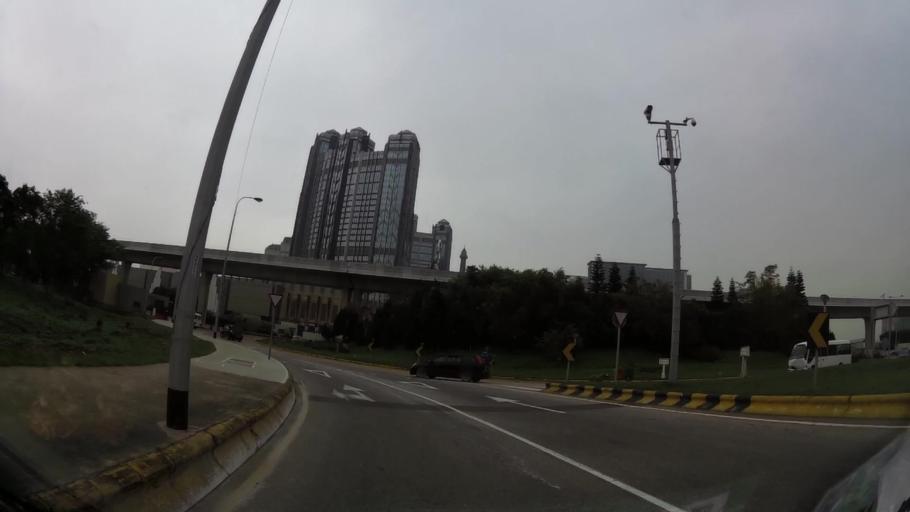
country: MO
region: Macau
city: Macau
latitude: 22.1381
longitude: 113.5631
